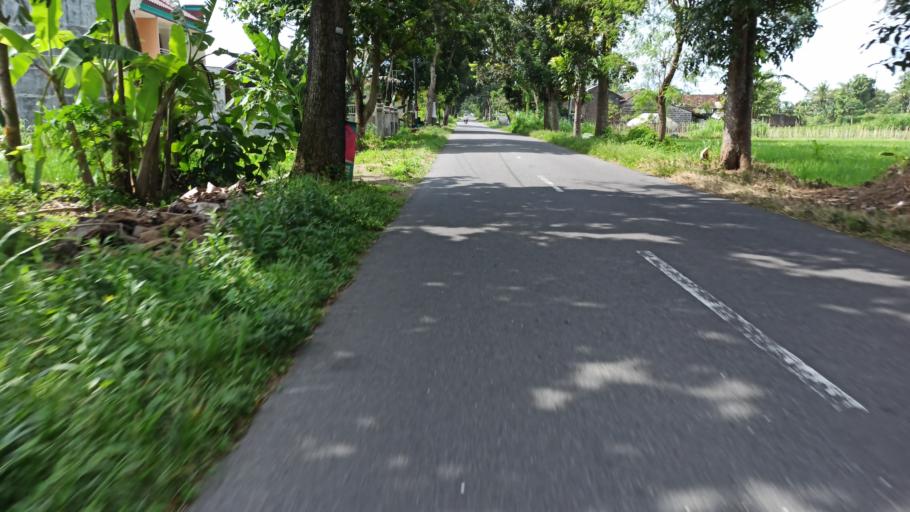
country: ID
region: Daerah Istimewa Yogyakarta
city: Sleman
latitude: -7.6911
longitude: 110.2954
